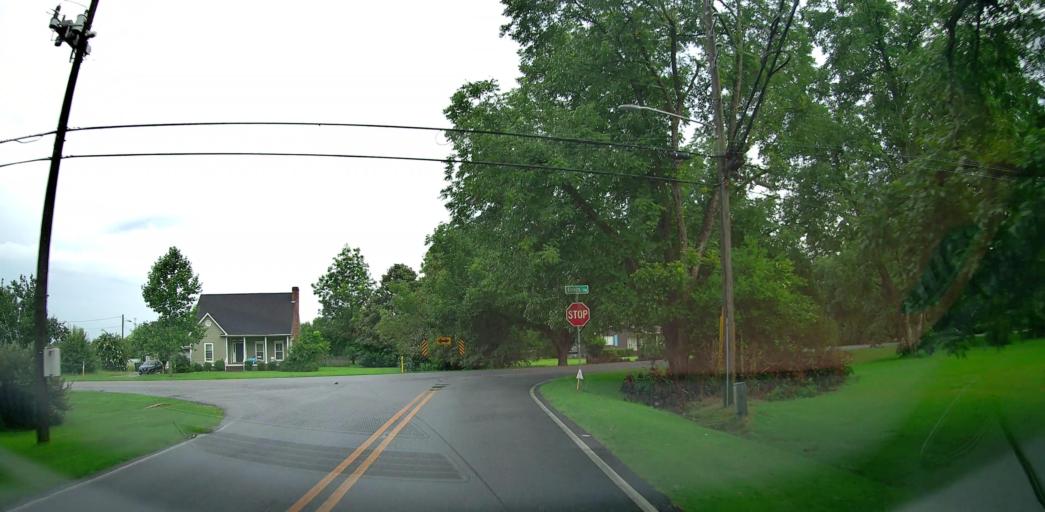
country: US
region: Georgia
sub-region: Peach County
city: Byron
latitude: 32.7315
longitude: -83.7040
